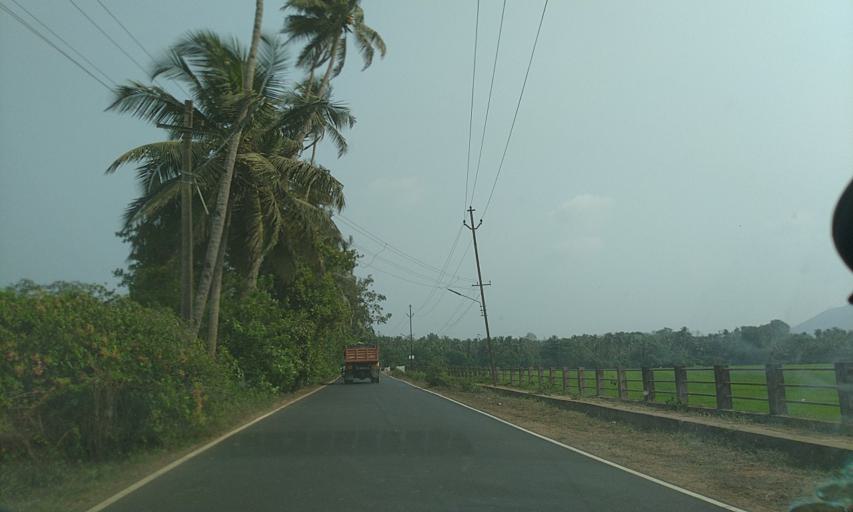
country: IN
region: Goa
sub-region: South Goa
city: Quepem
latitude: 15.2581
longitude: 74.0490
